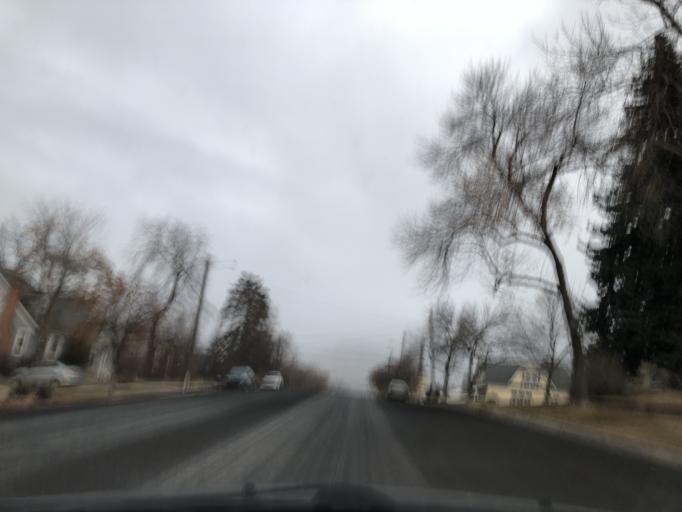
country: US
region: Utah
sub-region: Cache County
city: Logan
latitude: 41.7369
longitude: -111.8244
